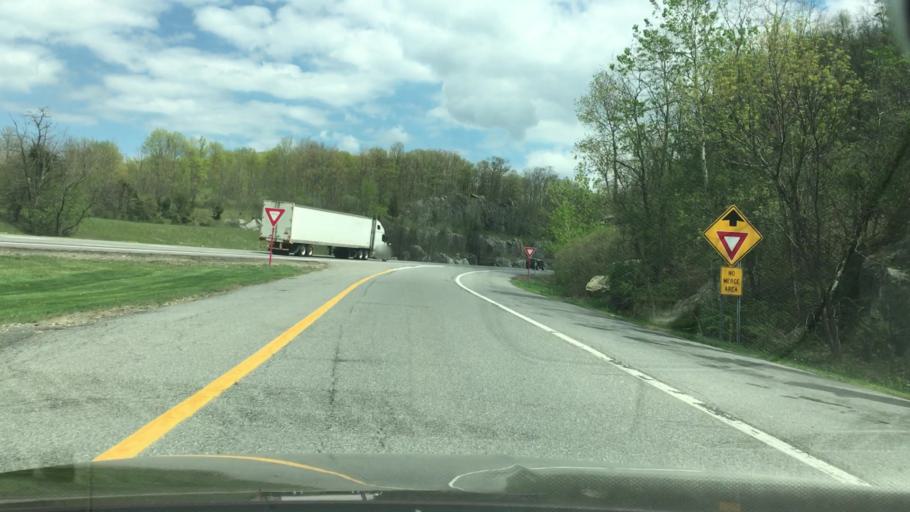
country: US
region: New York
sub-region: Putnam County
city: Lake Carmel
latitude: 41.5464
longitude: -73.7207
